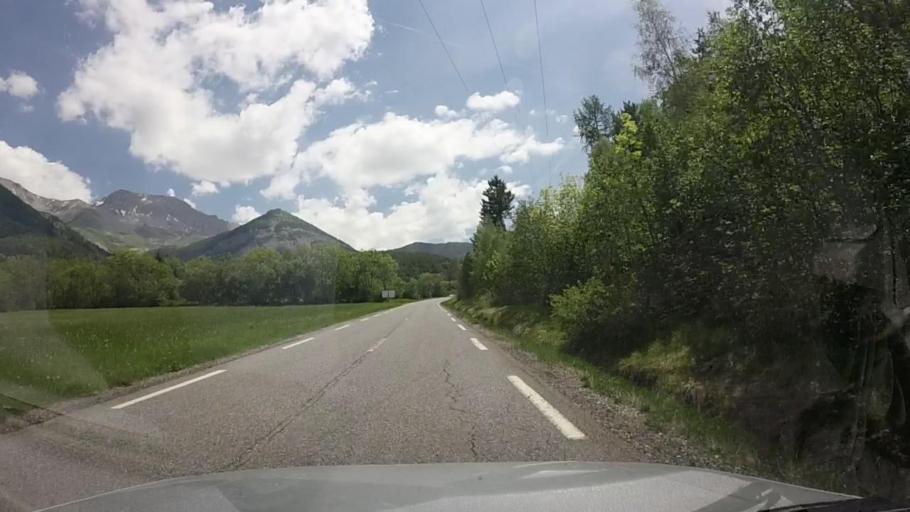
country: FR
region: Provence-Alpes-Cote d'Azur
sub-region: Departement des Alpes-de-Haute-Provence
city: Seyne-les-Alpes
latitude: 44.3221
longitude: 6.3993
